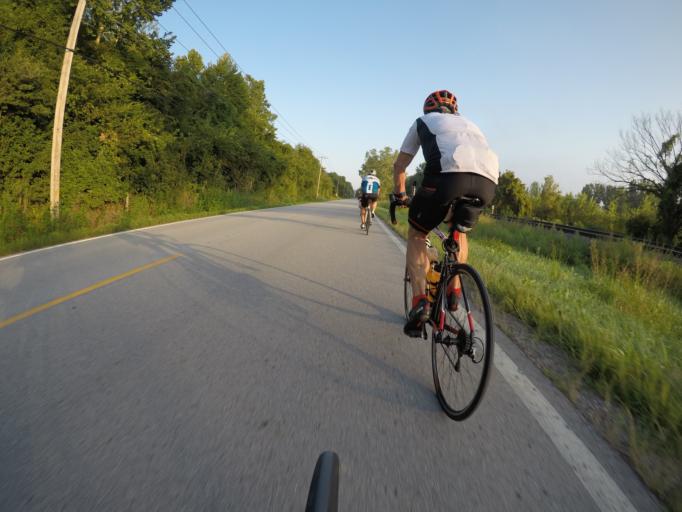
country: US
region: Kansas
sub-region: Leavenworth County
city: Lansing
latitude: 39.1917
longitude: -94.8054
